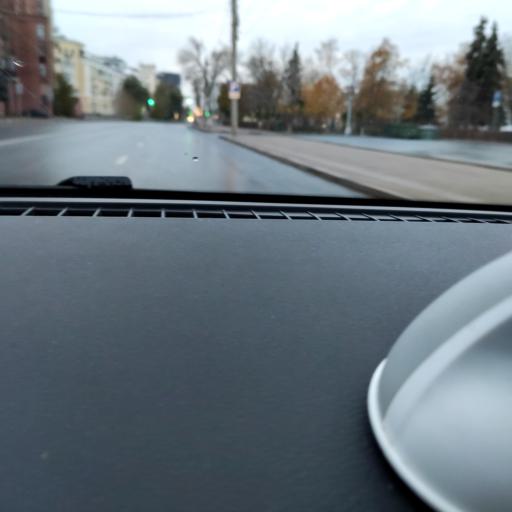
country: RU
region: Samara
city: Rozhdestveno
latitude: 53.1907
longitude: 50.0844
